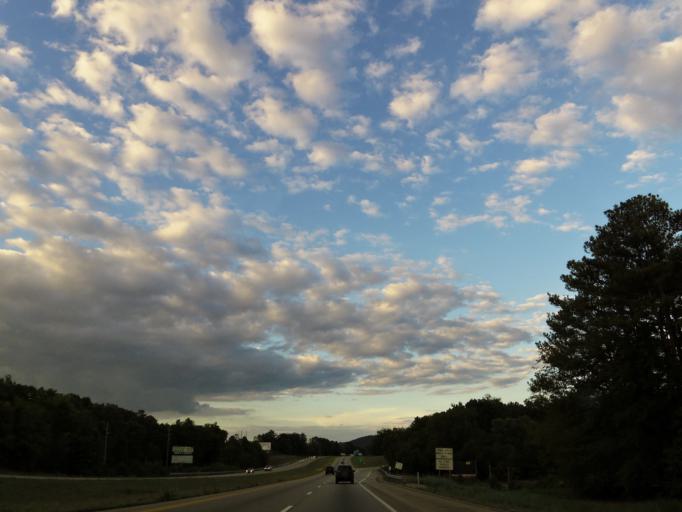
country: US
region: Tennessee
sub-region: Bradley County
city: Cleveland
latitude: 35.1806
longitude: -84.9116
